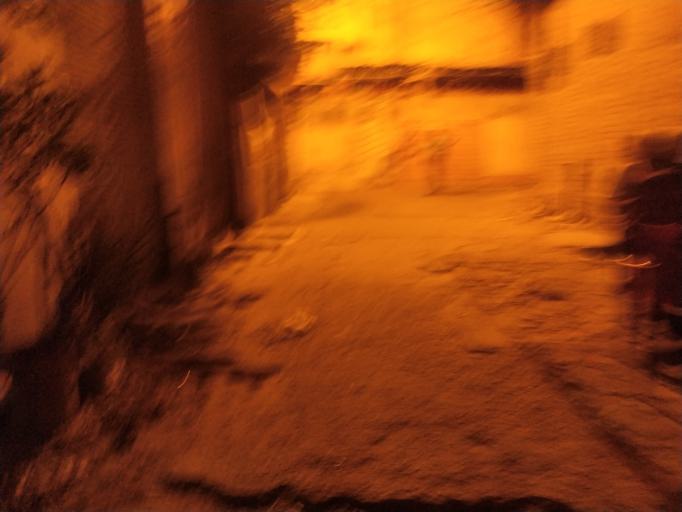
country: EG
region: Alexandria
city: Alexandria
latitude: 31.2130
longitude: 29.9241
